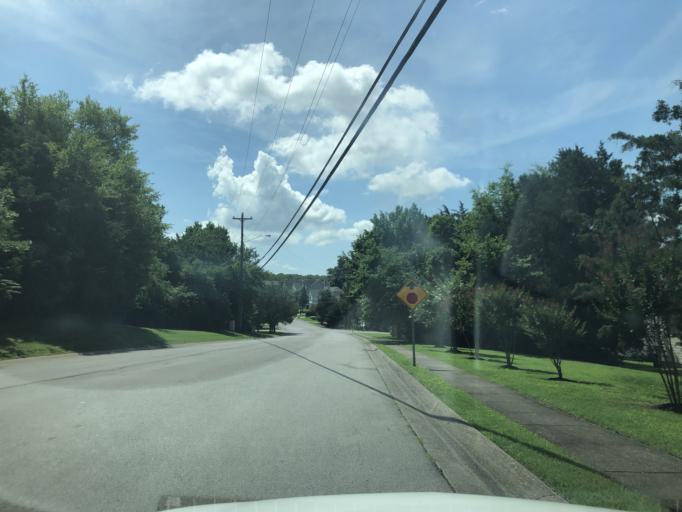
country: US
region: Tennessee
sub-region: Rutherford County
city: La Vergne
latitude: 36.0446
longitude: -86.6275
